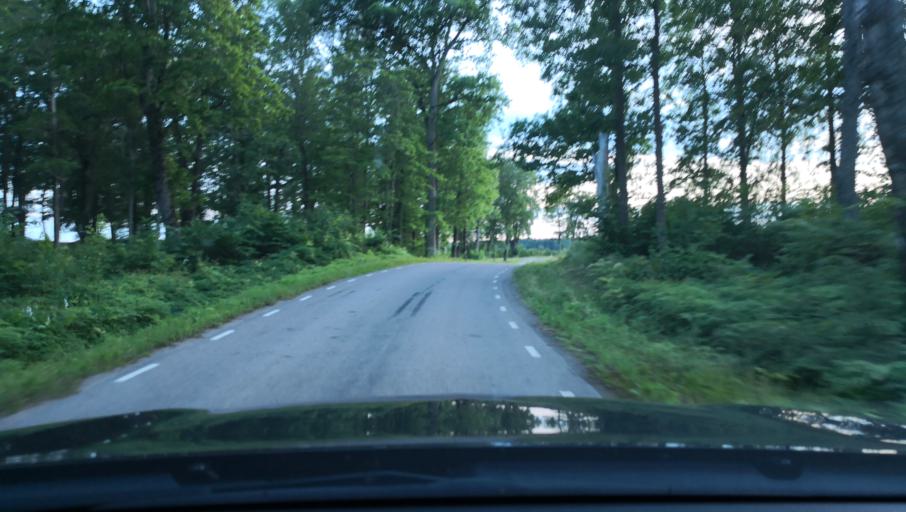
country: SE
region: Uppsala
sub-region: Osthammars Kommun
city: Bjorklinge
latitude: 60.0617
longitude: 17.5696
